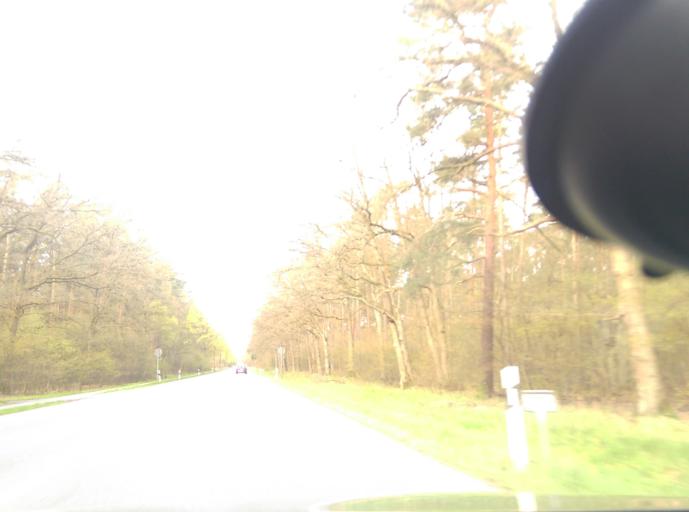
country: DE
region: Lower Saxony
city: Hambuhren
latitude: 52.6239
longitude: 10.0234
